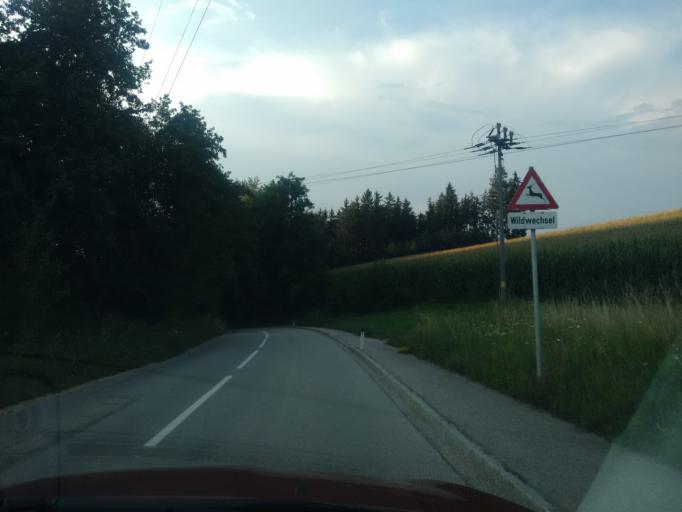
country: AT
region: Upper Austria
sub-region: Wels-Land
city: Offenhausen
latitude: 48.1682
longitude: 13.8591
